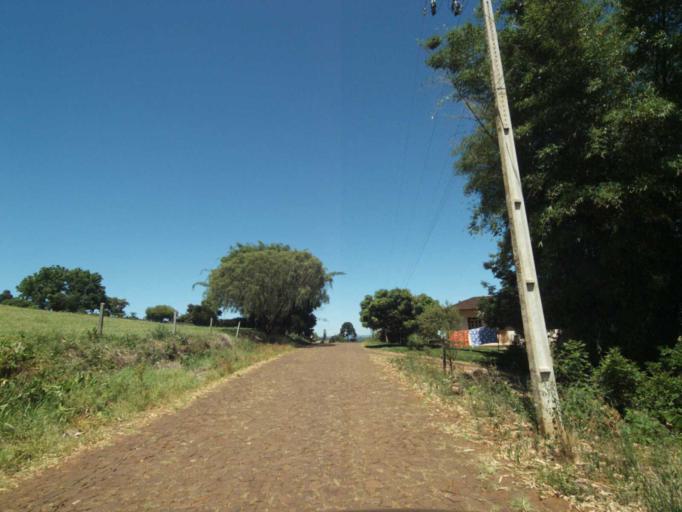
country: BR
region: Parana
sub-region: Coronel Vivida
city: Coronel Vivida
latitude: -25.9655
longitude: -52.8204
